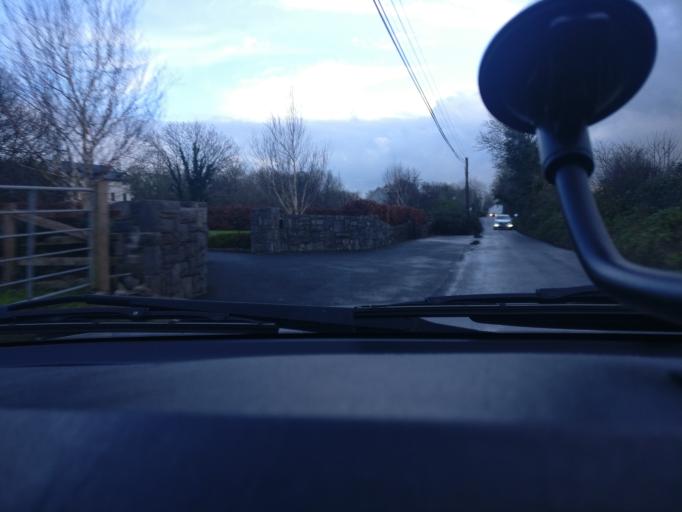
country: IE
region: Connaught
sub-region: County Galway
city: Athenry
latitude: 53.2079
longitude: -8.7166
